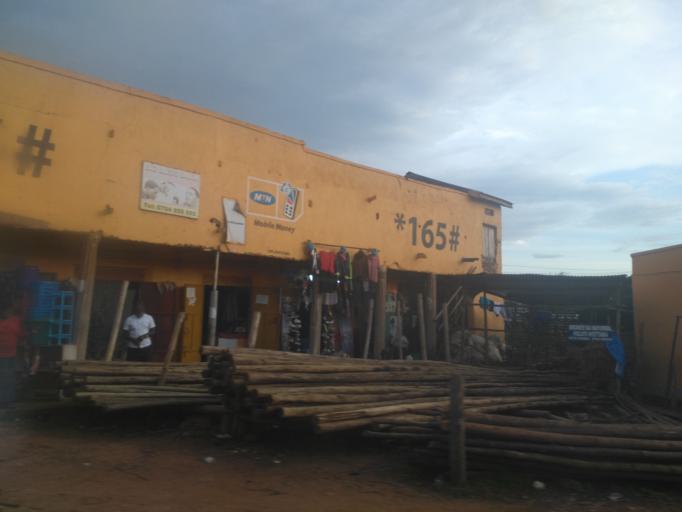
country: UG
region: Central Region
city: Kampala Central Division
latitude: 0.3820
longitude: 32.5653
